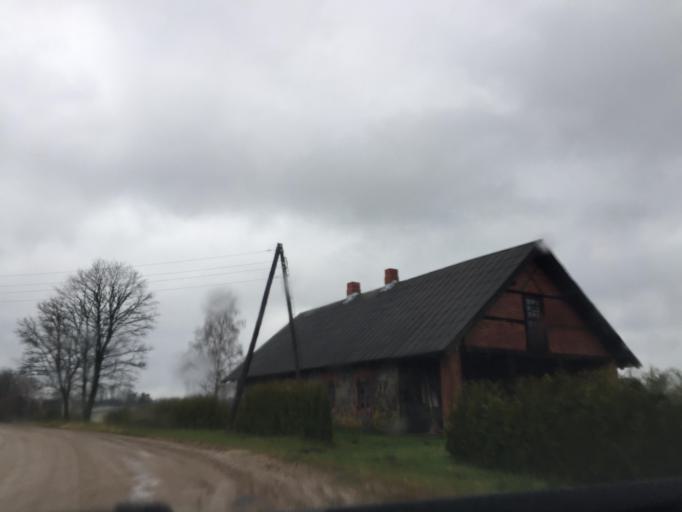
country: LV
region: Limbazu Rajons
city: Limbazi
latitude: 57.6518
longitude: 24.7772
